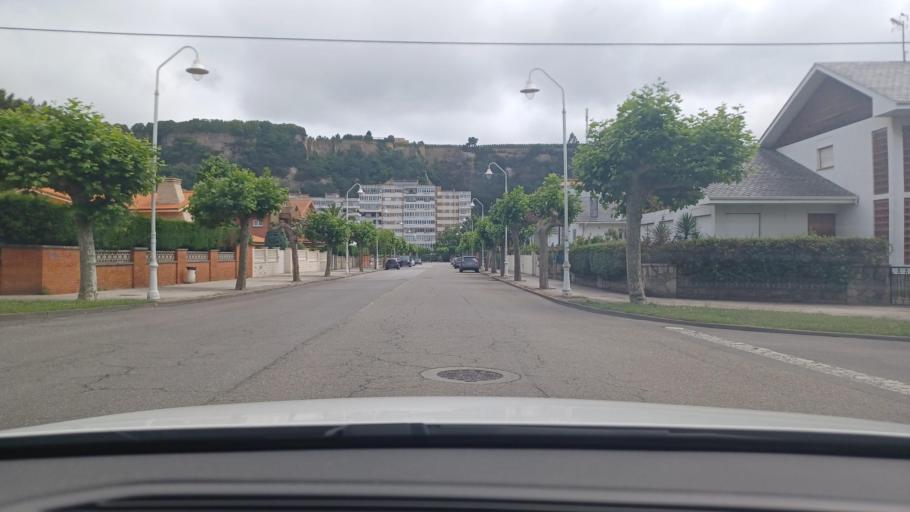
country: ES
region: Asturias
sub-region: Province of Asturias
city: Aviles
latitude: 43.5752
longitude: -5.9541
